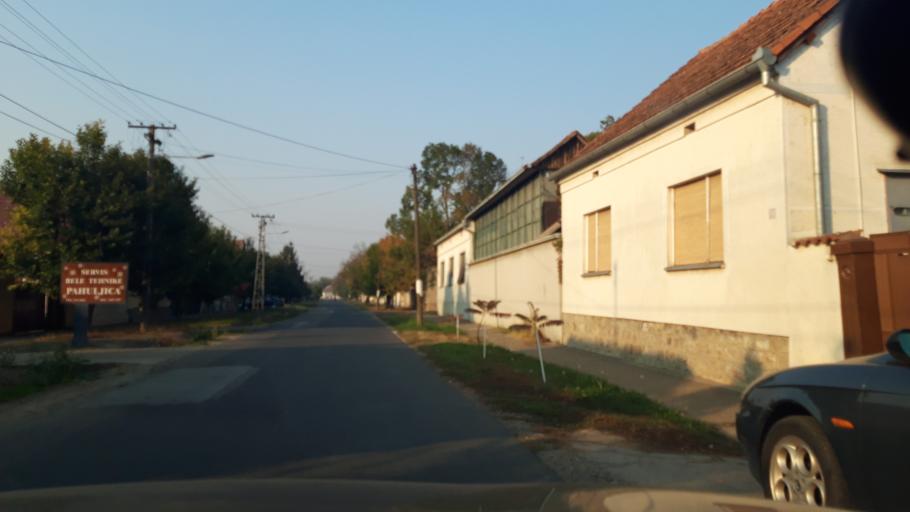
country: RS
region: Autonomna Pokrajina Vojvodina
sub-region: Sremski Okrug
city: Stara Pazova
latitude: 44.9874
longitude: 20.1500
